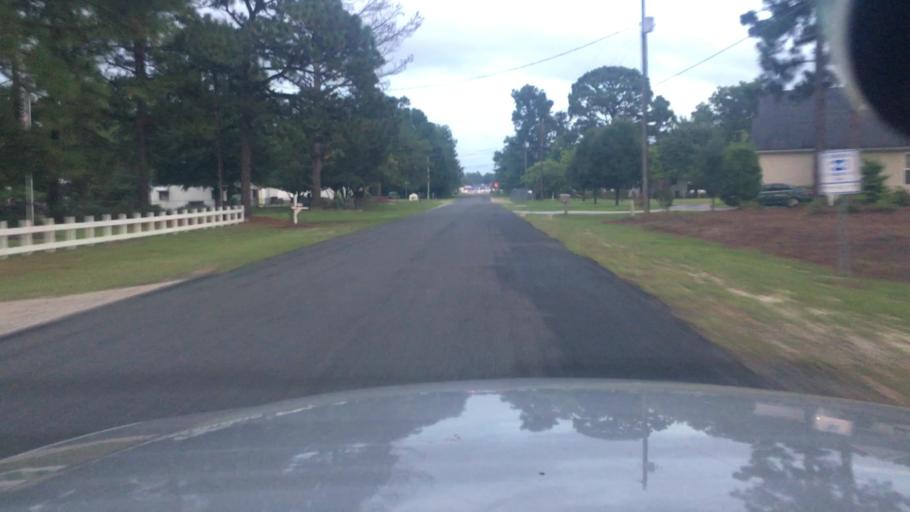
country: US
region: North Carolina
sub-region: Cumberland County
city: Hope Mills
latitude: 34.9840
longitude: -78.9110
